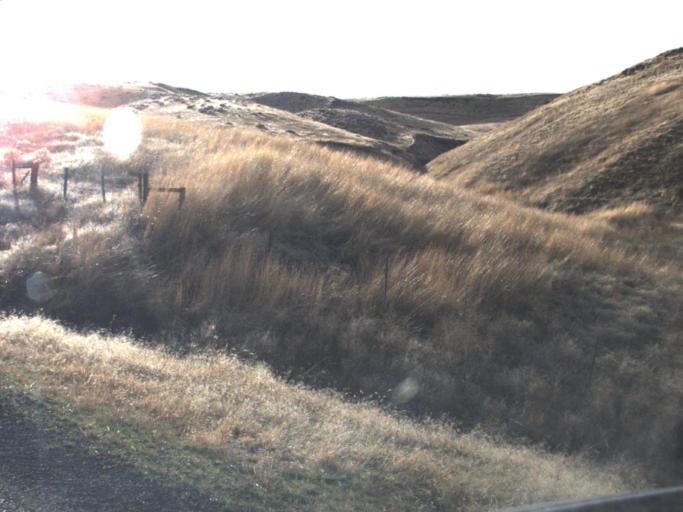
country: US
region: Washington
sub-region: Columbia County
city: Dayton
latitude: 46.4755
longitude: -117.9612
